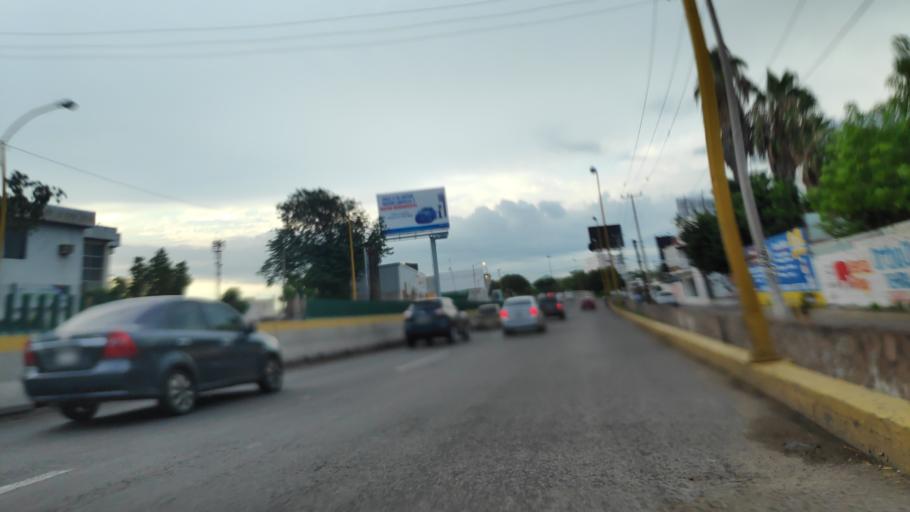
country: MX
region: Sinaloa
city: Culiacan
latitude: 24.8059
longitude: -107.4058
